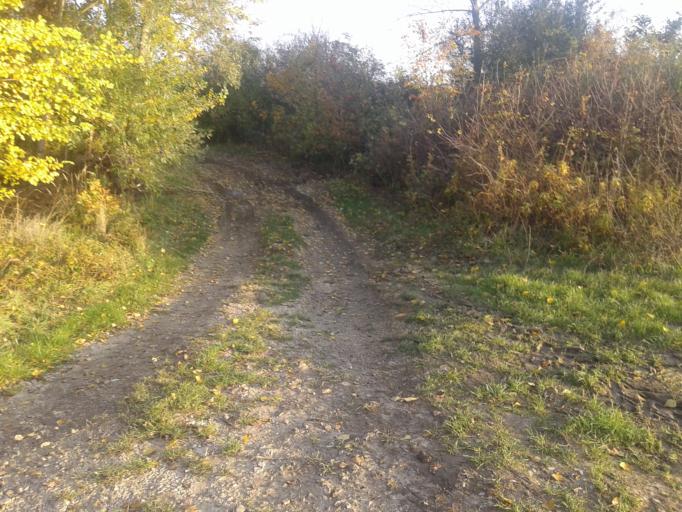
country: HU
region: Fejer
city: Fehervarcsurgo
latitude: 47.2896
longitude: 18.2554
